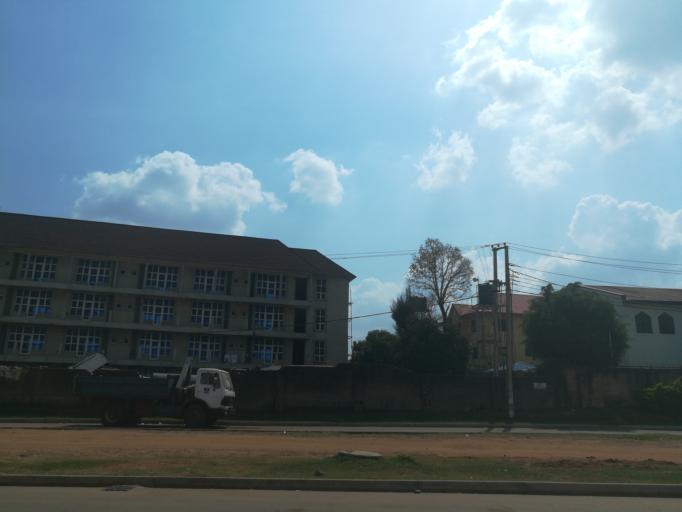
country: NG
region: Abuja Federal Capital Territory
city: Abuja
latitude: 9.0539
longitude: 7.4429
